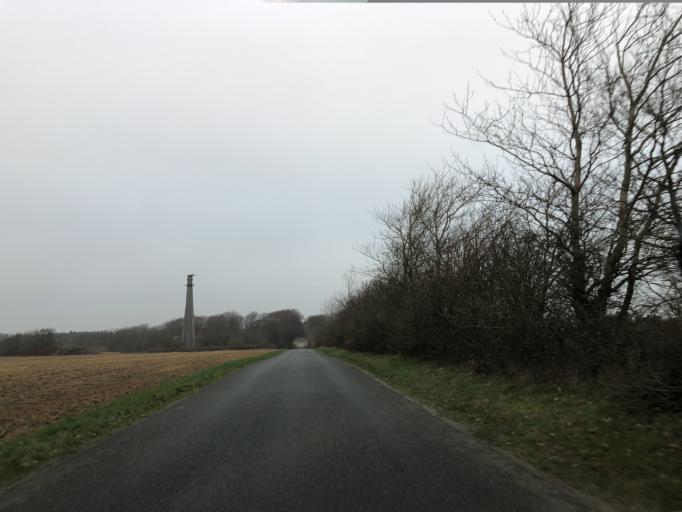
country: DK
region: Central Jutland
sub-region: Holstebro Kommune
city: Ulfborg
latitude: 56.1987
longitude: 8.3133
